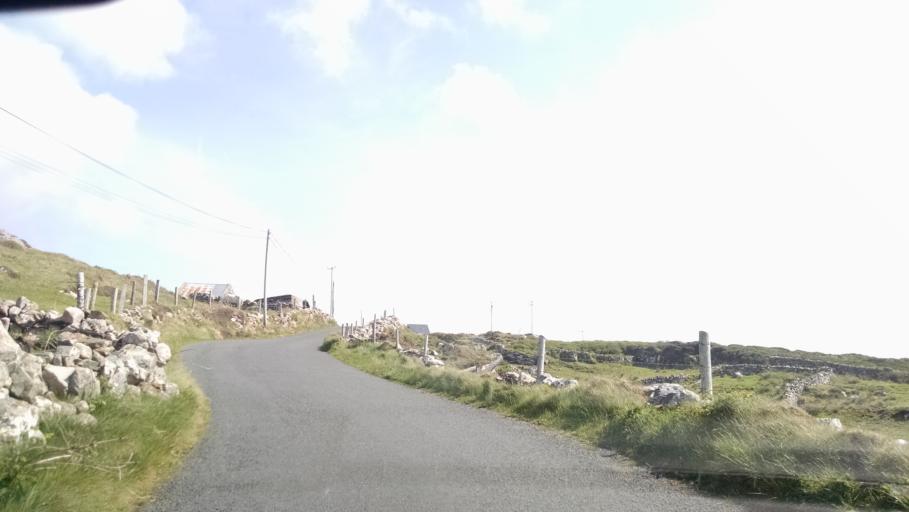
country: IE
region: Connaught
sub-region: County Galway
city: Clifden
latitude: 53.5086
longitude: -10.1138
